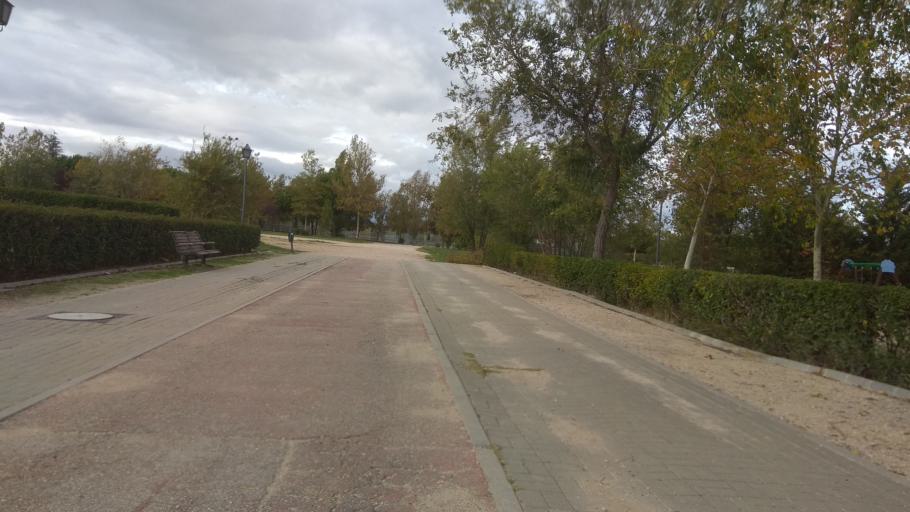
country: ES
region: Madrid
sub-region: Provincia de Madrid
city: Vicalvaro
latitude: 40.4096
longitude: -3.6156
